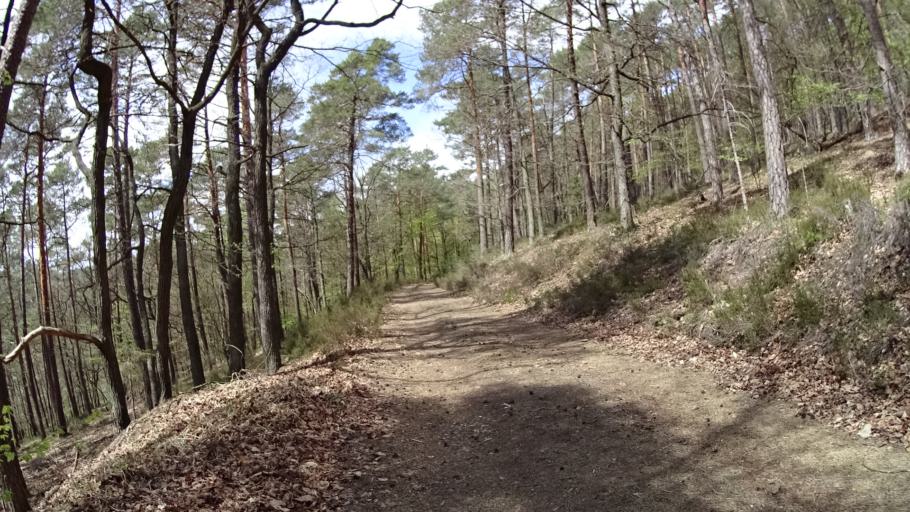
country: DE
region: Rheinland-Pfalz
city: Ramberg
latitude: 49.3066
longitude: 8.0100
